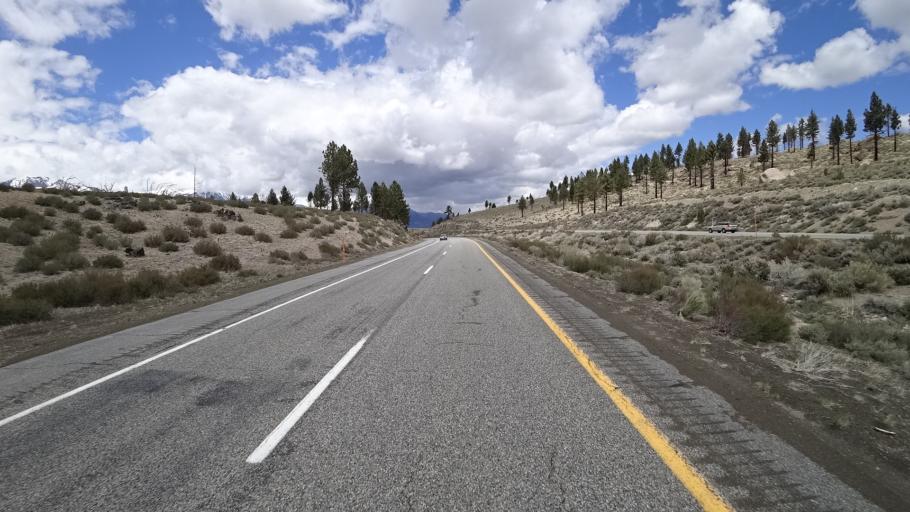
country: US
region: California
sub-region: Mono County
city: Mammoth Lakes
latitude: 37.8257
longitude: -119.0643
